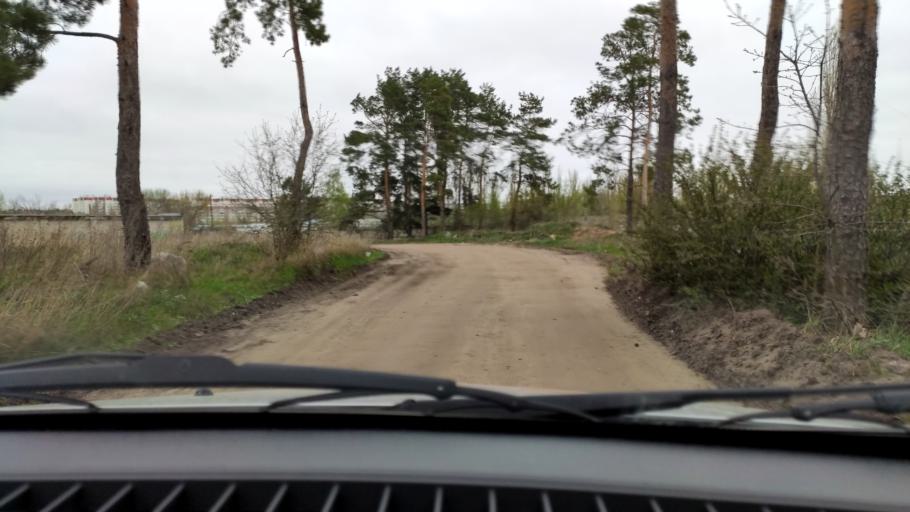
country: RU
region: Voronezj
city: Pridonskoy
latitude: 51.6177
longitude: 39.0692
